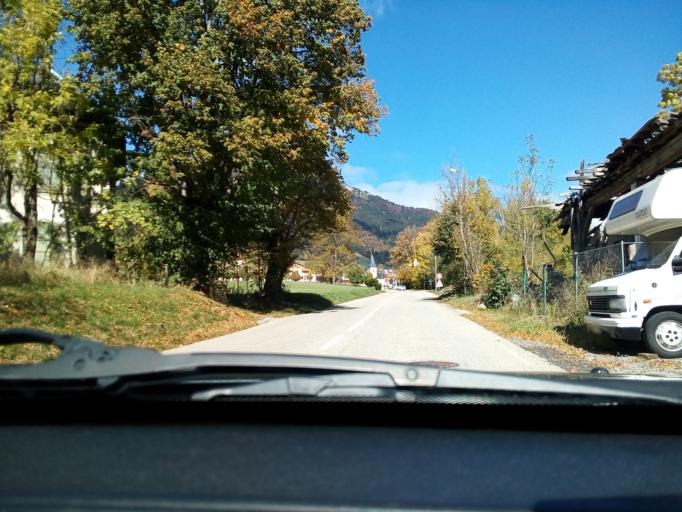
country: FR
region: Rhone-Alpes
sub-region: Departement de l'Isere
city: Le Sappey-en-Chartreuse
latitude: 45.2570
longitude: 5.7756
